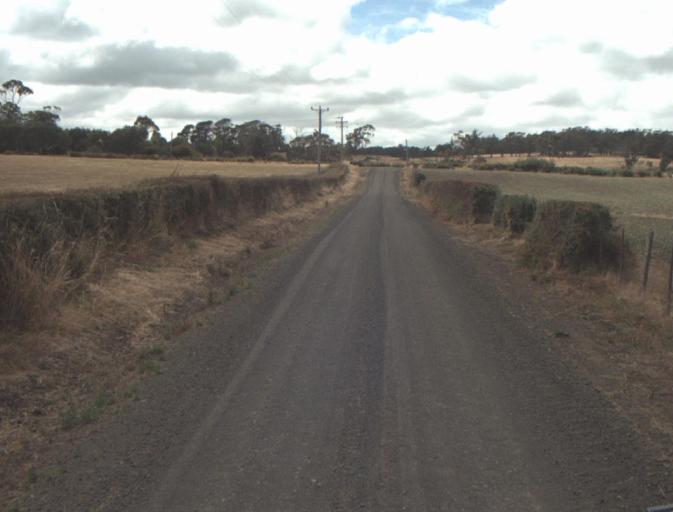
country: AU
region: Tasmania
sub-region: Northern Midlands
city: Evandale
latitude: -41.5173
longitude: 147.2919
